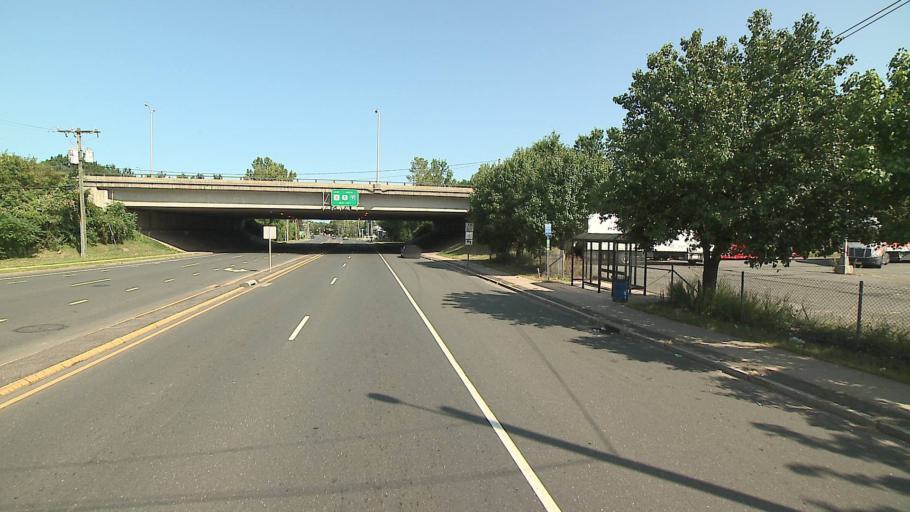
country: US
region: Connecticut
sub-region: Hartford County
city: East Hartford
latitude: 41.7581
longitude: -72.6435
